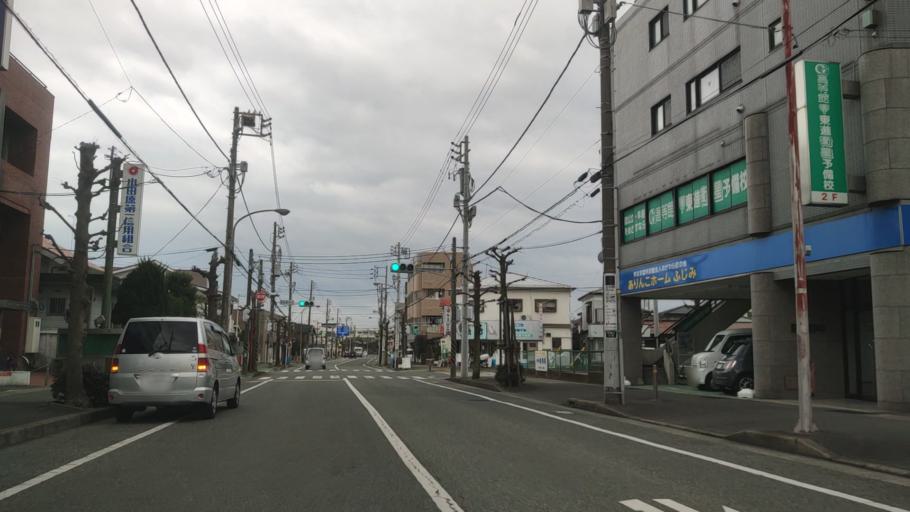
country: JP
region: Kanagawa
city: Odawara
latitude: 35.2748
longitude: 139.1804
